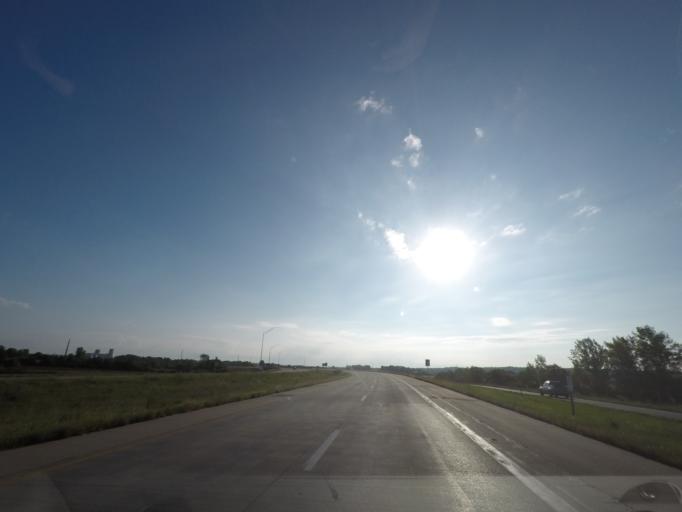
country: US
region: Iowa
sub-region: Warren County
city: Carlisle
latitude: 41.5112
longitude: -93.5292
